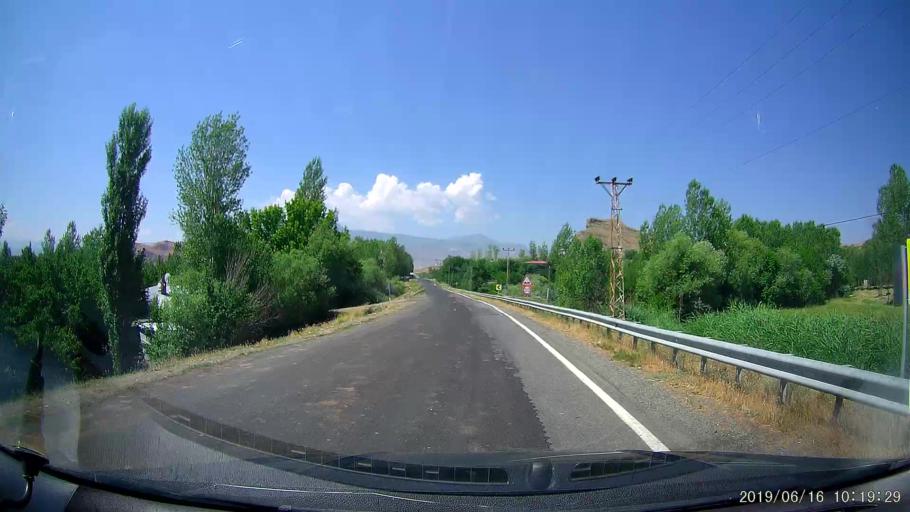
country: TR
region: Igdir
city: Tuzluca
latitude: 40.1547
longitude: 43.6558
